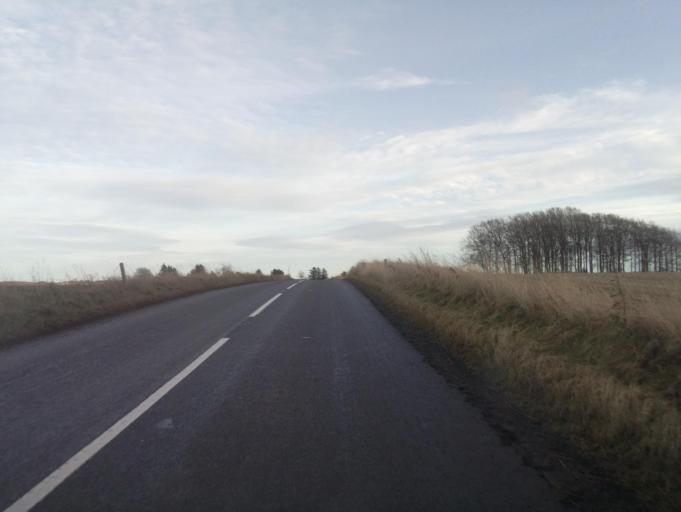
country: GB
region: Scotland
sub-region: Angus
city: Letham
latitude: 56.5794
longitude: -2.7928
